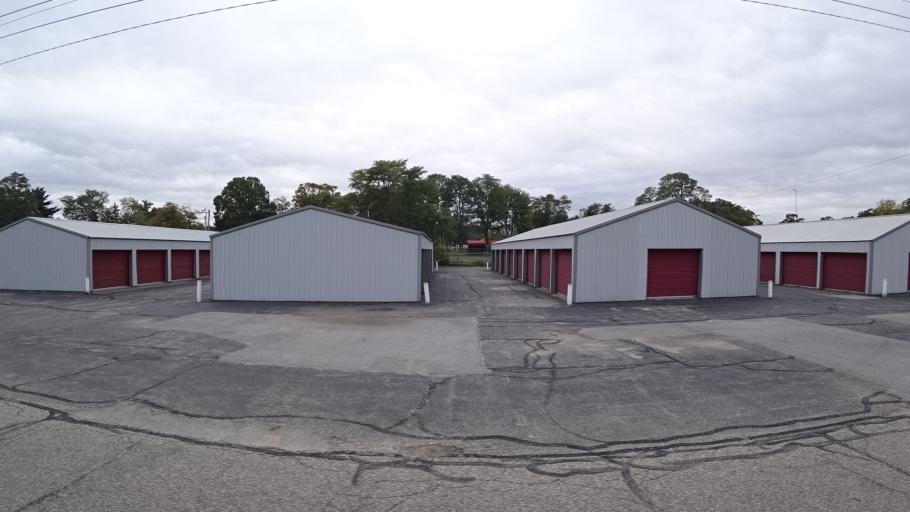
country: US
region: Indiana
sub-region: LaPorte County
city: Michigan City
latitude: 41.7008
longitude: -86.8877
